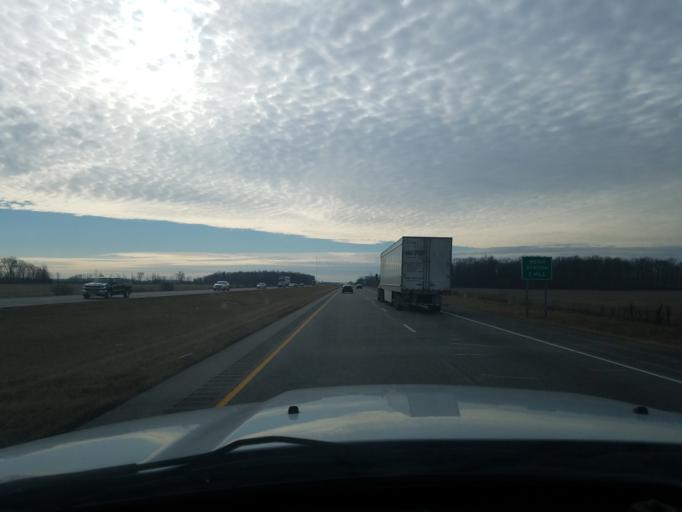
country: US
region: Indiana
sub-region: Huntington County
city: Markle
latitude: 40.7628
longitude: -85.3963
